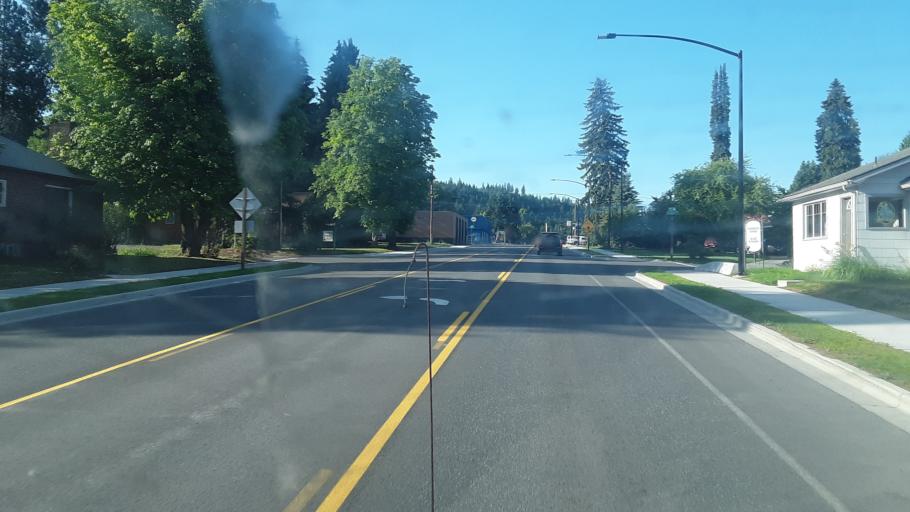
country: US
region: Idaho
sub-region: Boundary County
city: Bonners Ferry
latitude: 48.6900
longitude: -116.3163
